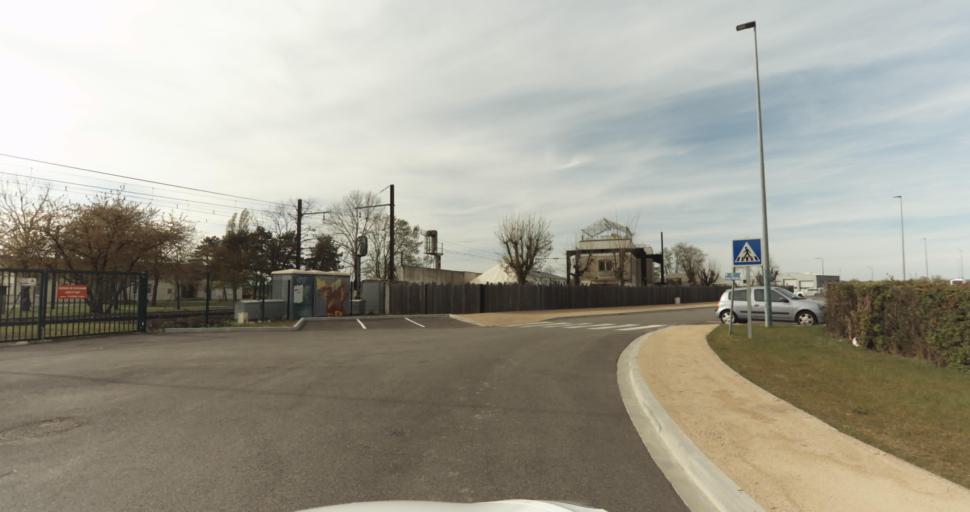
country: FR
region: Rhone-Alpes
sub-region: Departement de l'Ain
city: Amberieu-en-Bugey
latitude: 45.9779
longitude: 5.3452
